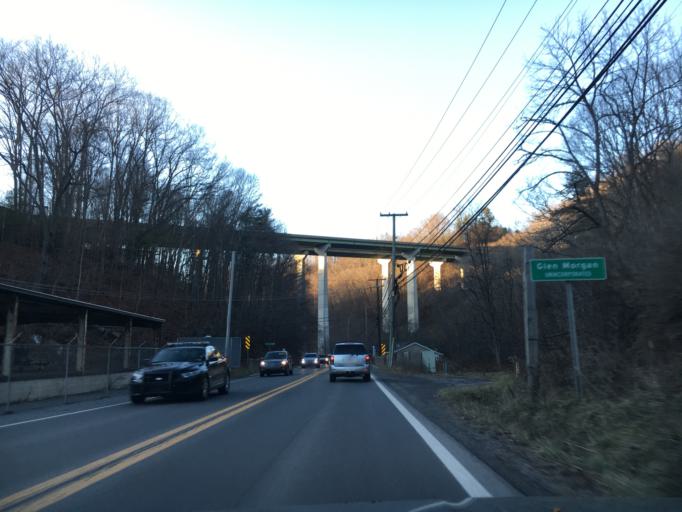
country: US
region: West Virginia
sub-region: Raleigh County
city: Beaver
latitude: 37.7538
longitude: -81.1489
